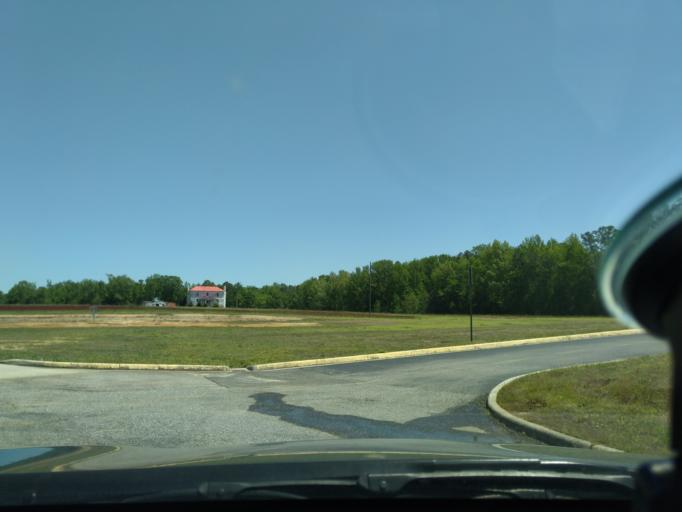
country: US
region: Virginia
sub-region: Prince George County
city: Prince George
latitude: 37.2145
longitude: -77.3052
